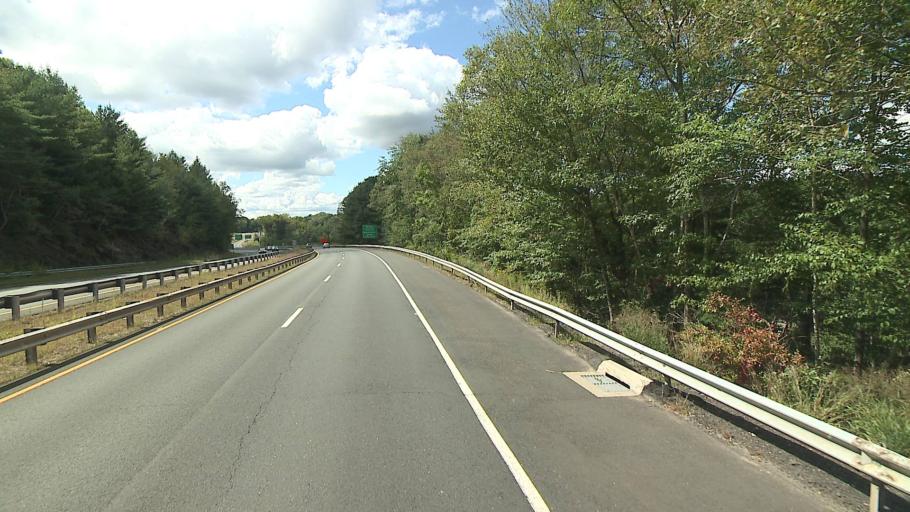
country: US
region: Connecticut
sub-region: Hartford County
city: Manchester
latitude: 41.7893
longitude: -72.4493
